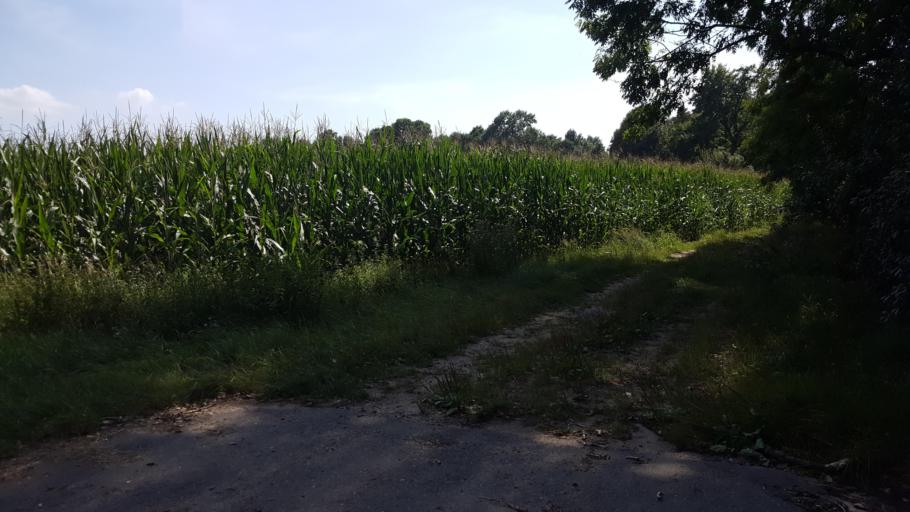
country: BY
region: Brest
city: Kamyanyuki
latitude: 52.4909
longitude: 23.6857
